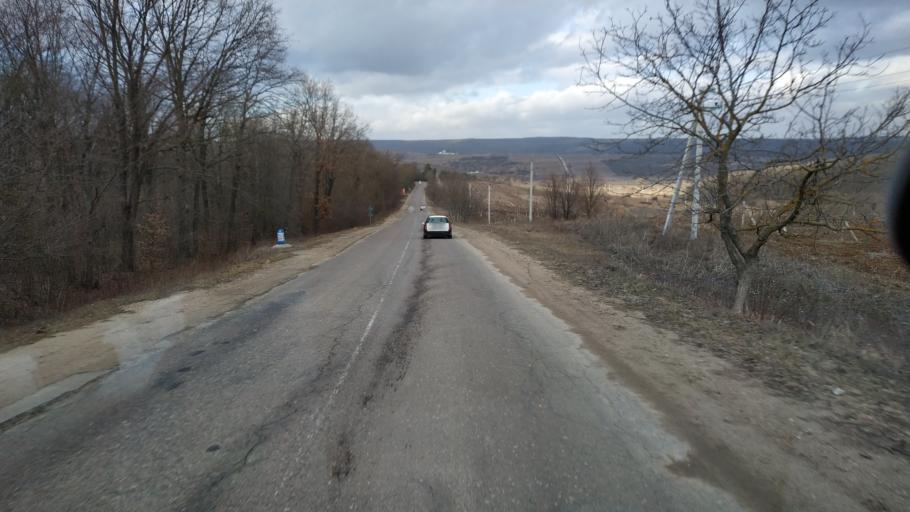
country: MD
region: Calarasi
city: Calarasi
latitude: 47.3011
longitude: 28.3712
